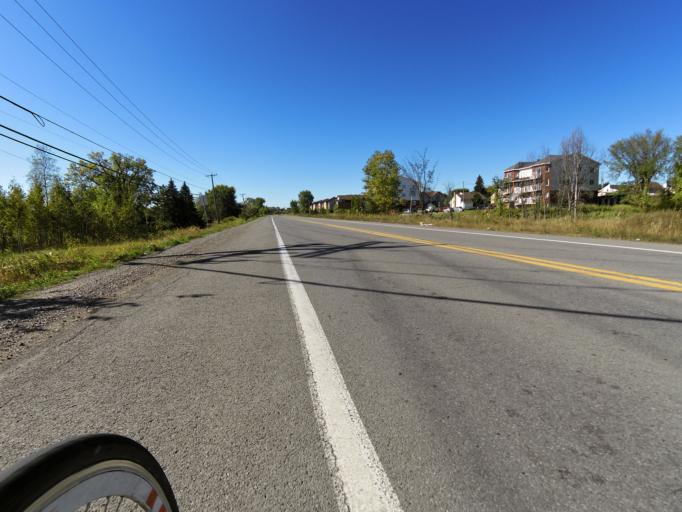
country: CA
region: Ontario
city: Clarence-Rockland
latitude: 45.5268
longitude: -75.4797
